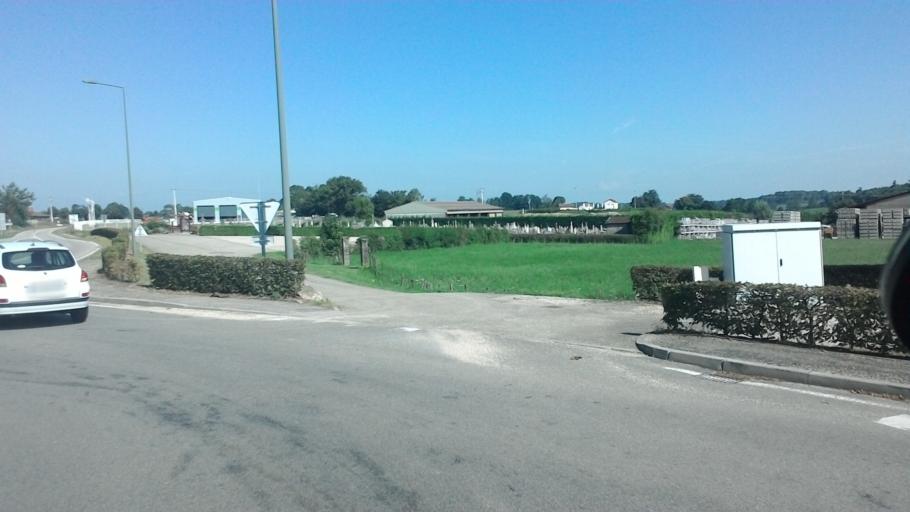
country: FR
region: Rhone-Alpes
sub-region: Departement de l'Ain
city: Saint-Trivier-de-Courtes
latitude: 46.4603
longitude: 5.0834
